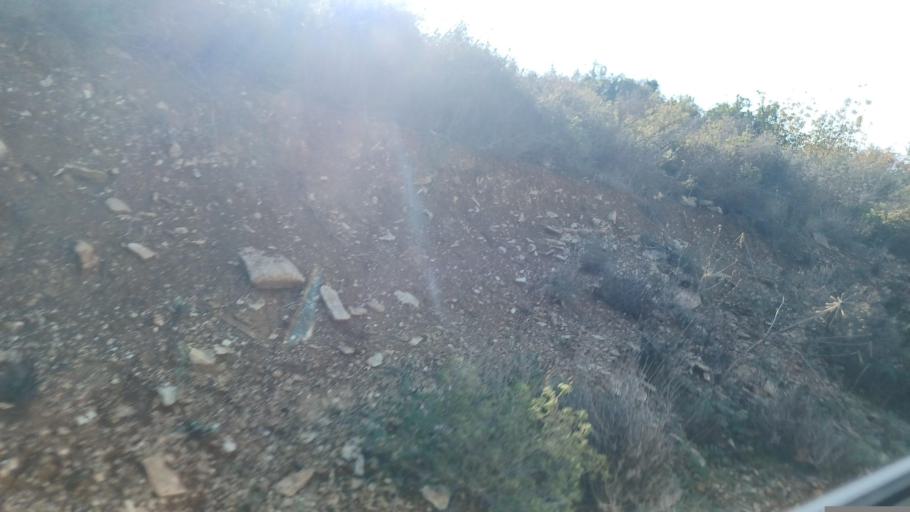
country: CY
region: Larnaka
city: Kofinou
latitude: 34.8439
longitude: 33.2960
